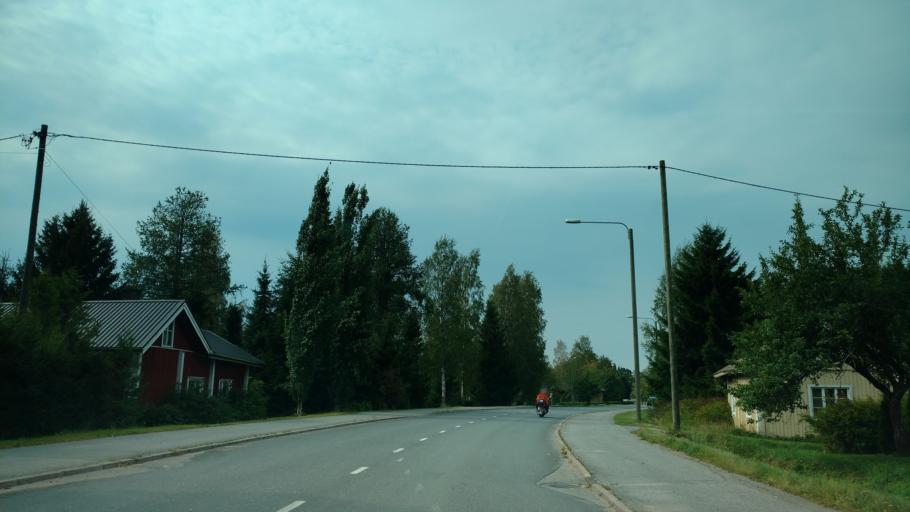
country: FI
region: Varsinais-Suomi
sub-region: Loimaa
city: Koski Tl
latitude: 60.6581
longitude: 23.1454
